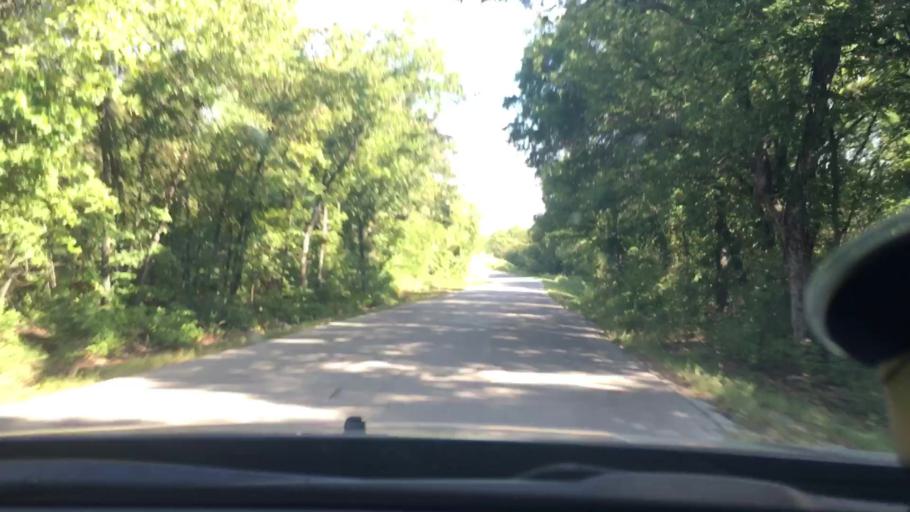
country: US
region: Oklahoma
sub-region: Carter County
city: Lone Grove
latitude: 34.2806
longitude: -97.2824
